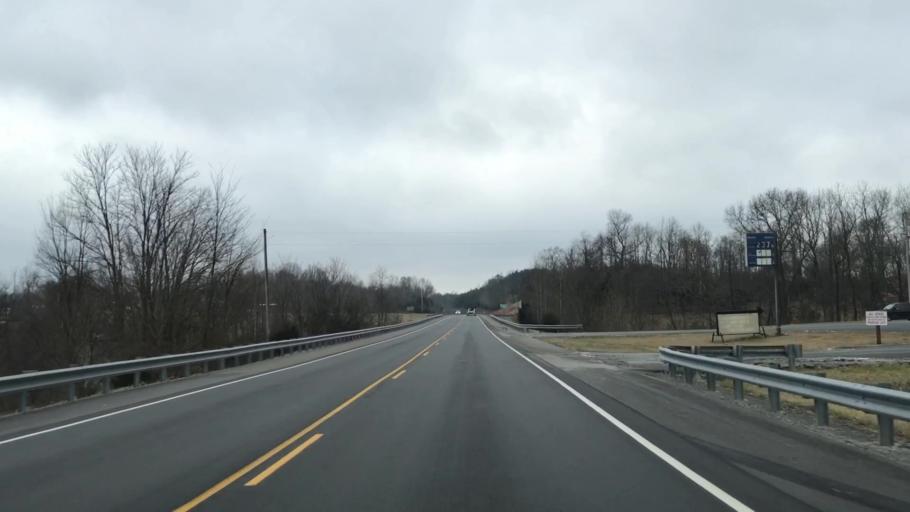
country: US
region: Kentucky
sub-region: Metcalfe County
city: Edmonton
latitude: 36.9552
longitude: -85.4411
